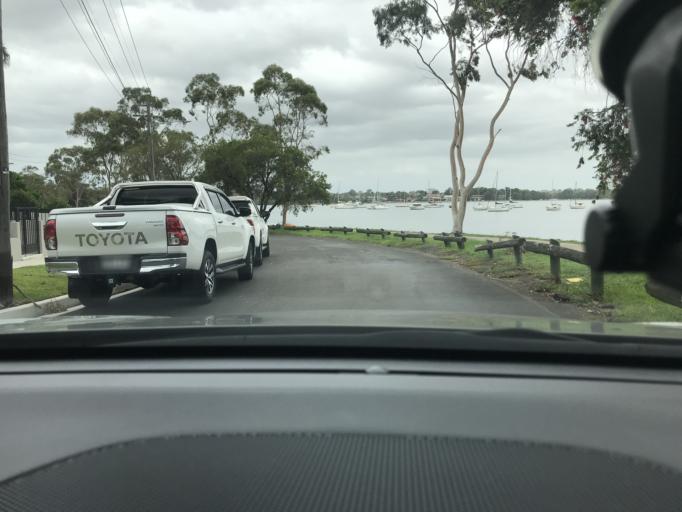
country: AU
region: New South Wales
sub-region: Canada Bay
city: Wareemba
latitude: -33.8539
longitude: 151.1262
